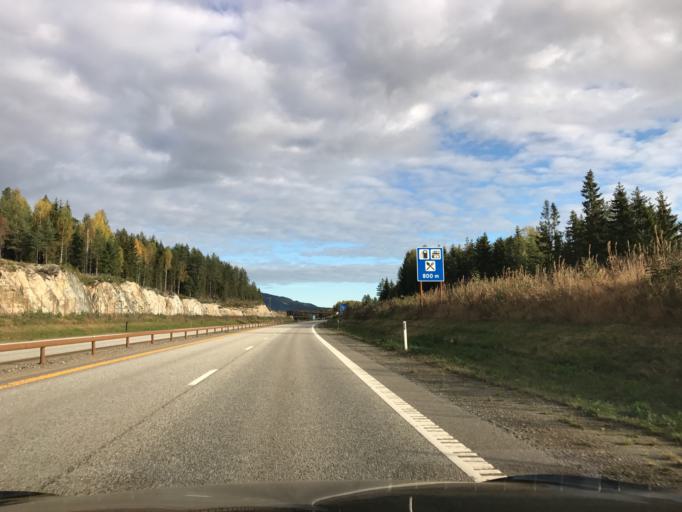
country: NO
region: Akershus
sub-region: Eidsvoll
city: Raholt
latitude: 60.3003
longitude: 11.1388
